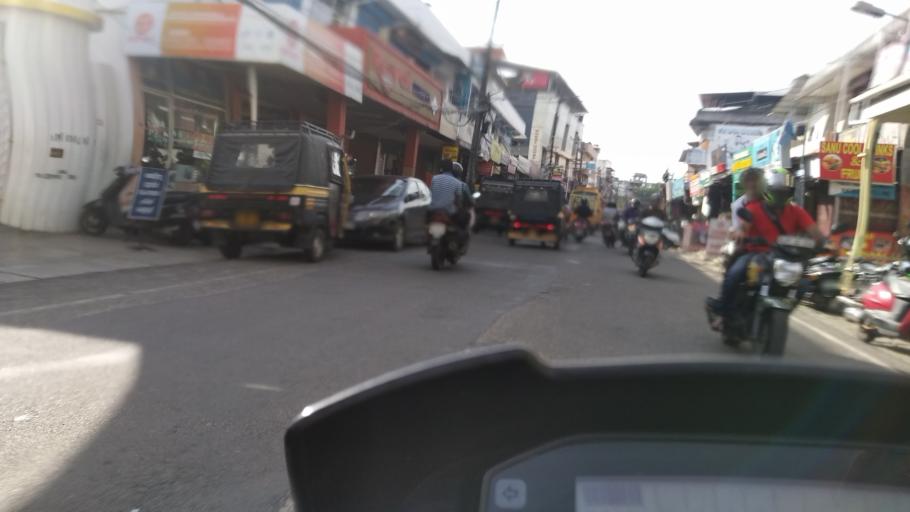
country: IN
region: Kerala
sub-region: Ernakulam
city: Elur
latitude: 10.0047
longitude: 76.2952
